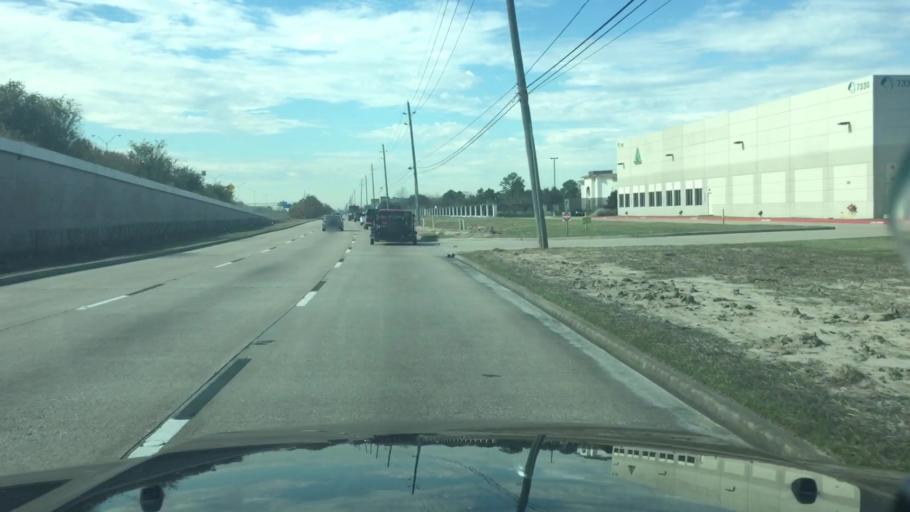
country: US
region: Texas
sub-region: Harris County
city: Hudson
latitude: 29.9360
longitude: -95.5304
